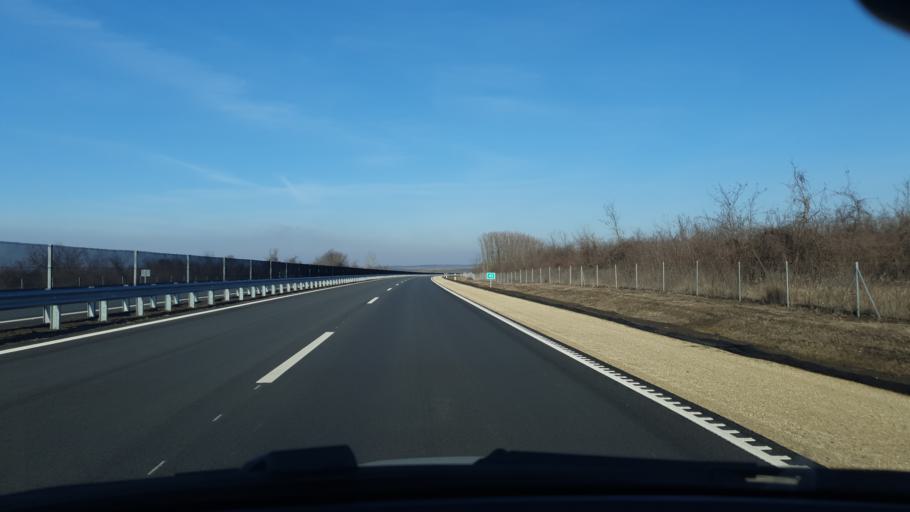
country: HU
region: Pest
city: Gomba
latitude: 47.3414
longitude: 19.5009
